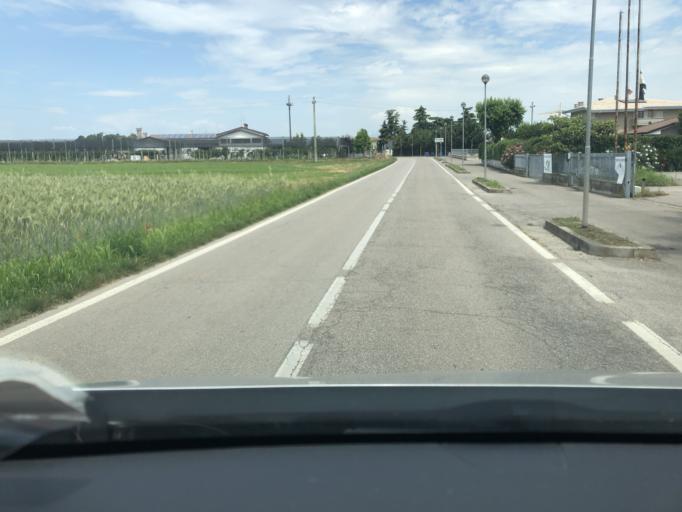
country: IT
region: Veneto
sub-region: Provincia di Verona
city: Valeggio sul Mincio
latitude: 45.3414
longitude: 10.7342
